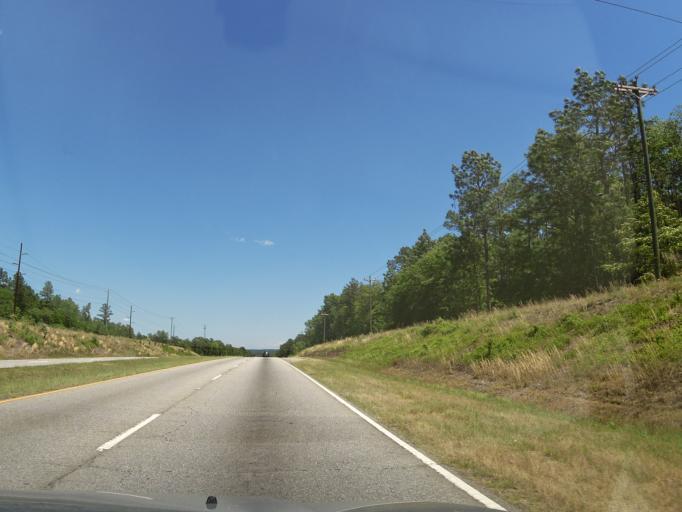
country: US
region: South Carolina
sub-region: Aiken County
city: Clearwater
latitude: 33.5066
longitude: -81.8876
